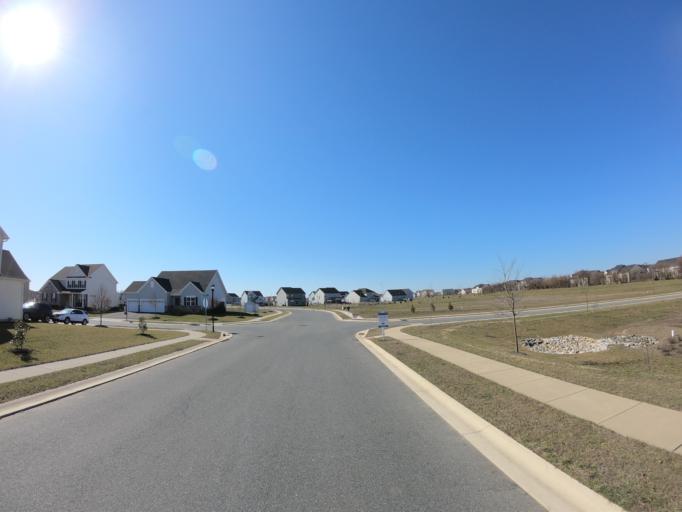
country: US
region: Delaware
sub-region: New Castle County
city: Middletown
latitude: 39.5183
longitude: -75.6576
